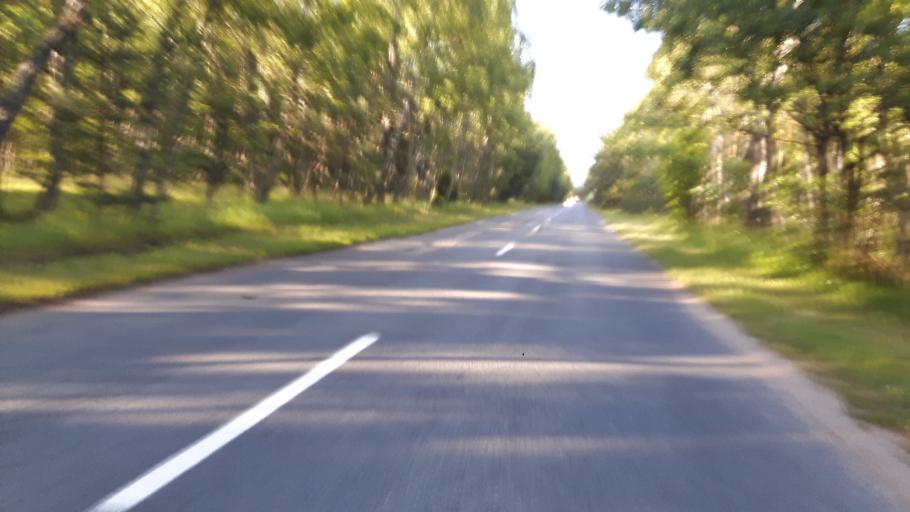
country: LT
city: Nida
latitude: 55.2344
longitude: 20.9064
